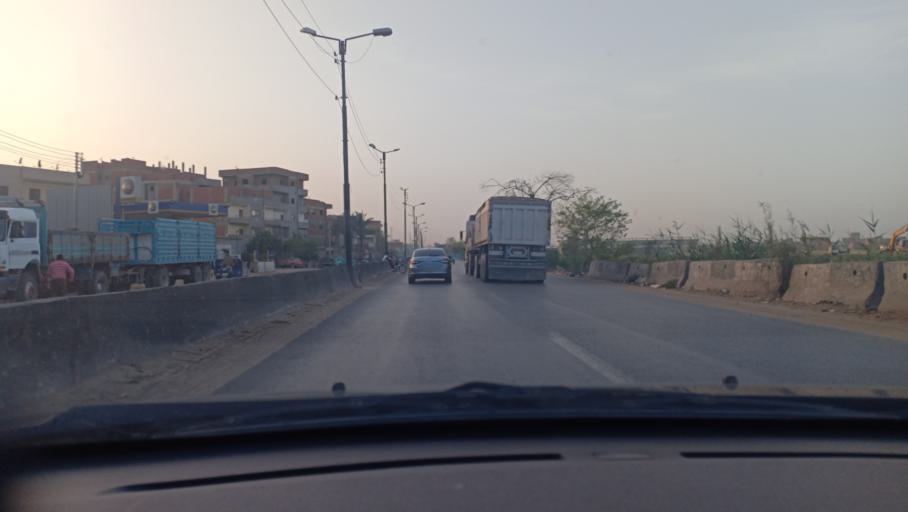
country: EG
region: Muhafazat al Gharbiyah
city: Zifta
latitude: 30.6835
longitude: 31.2810
